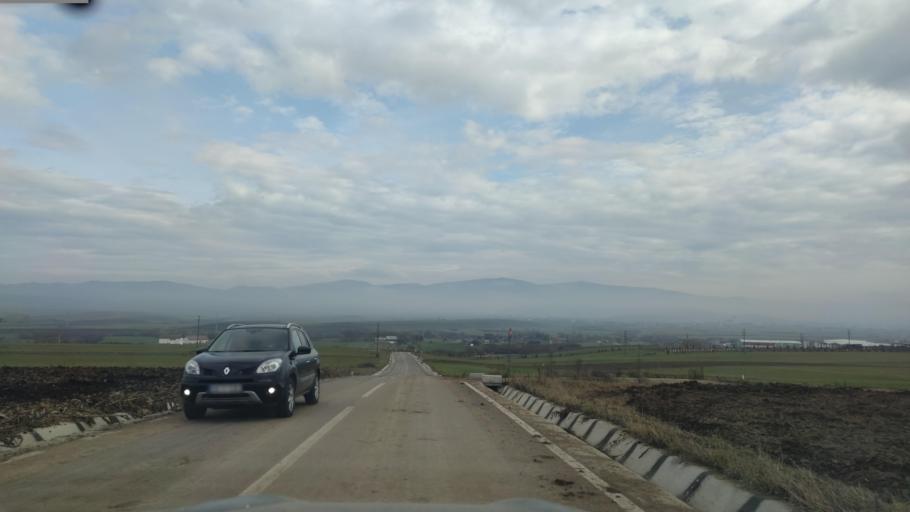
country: RO
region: Harghita
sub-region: Comuna Subcetate
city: Subcetate
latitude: 46.8184
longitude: 25.4505
